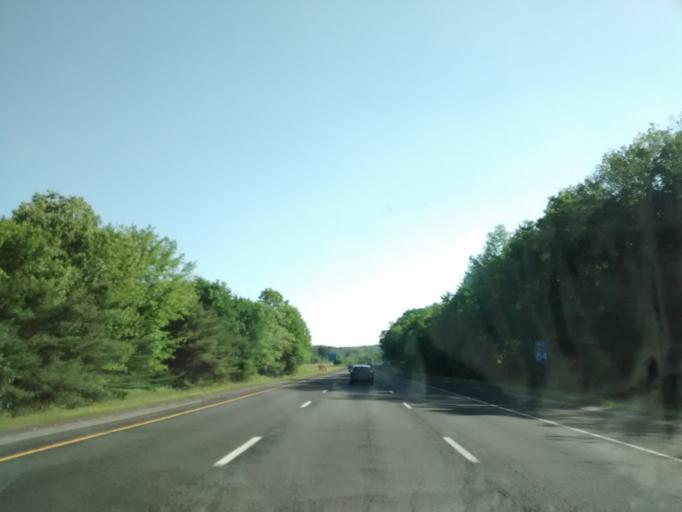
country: US
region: Massachusetts
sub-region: Hampden County
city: Holland
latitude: 42.0330
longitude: -72.1345
